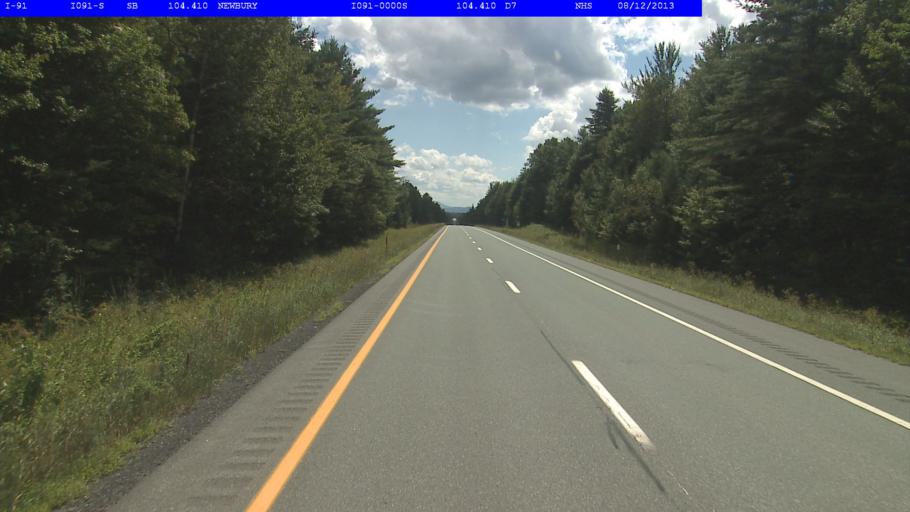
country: US
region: New Hampshire
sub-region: Grafton County
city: Haverhill
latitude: 44.0773
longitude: -72.1132
